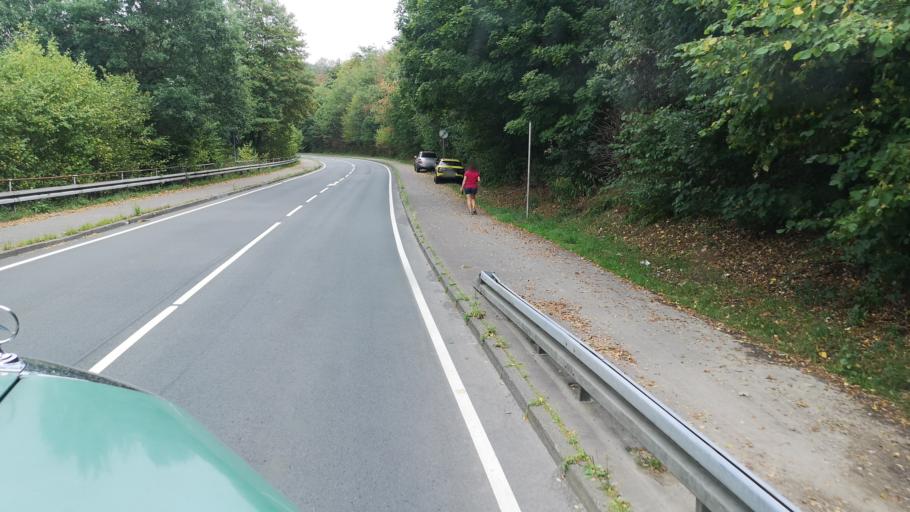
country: DE
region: North Rhine-Westphalia
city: Huckeswagen
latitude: 51.1855
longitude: 7.3096
